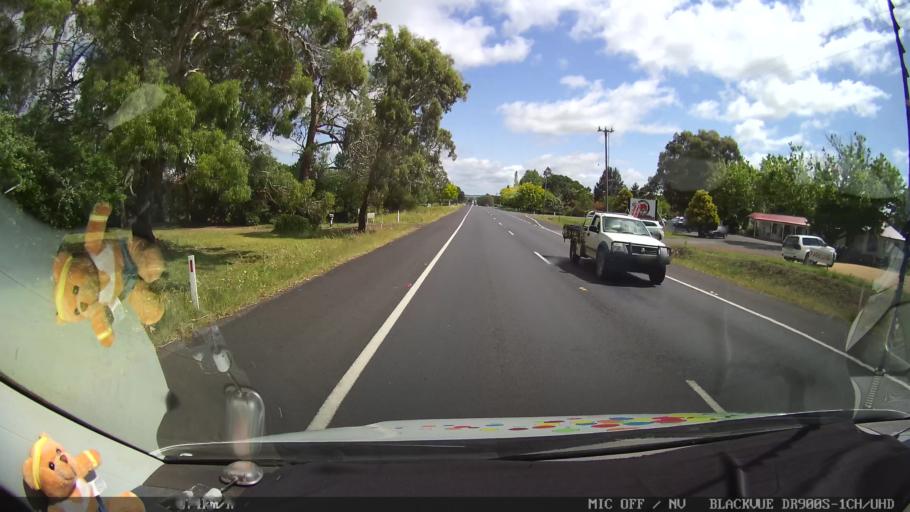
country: AU
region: New South Wales
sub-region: Glen Innes Severn
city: Glen Innes
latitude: -29.7618
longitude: 151.7337
